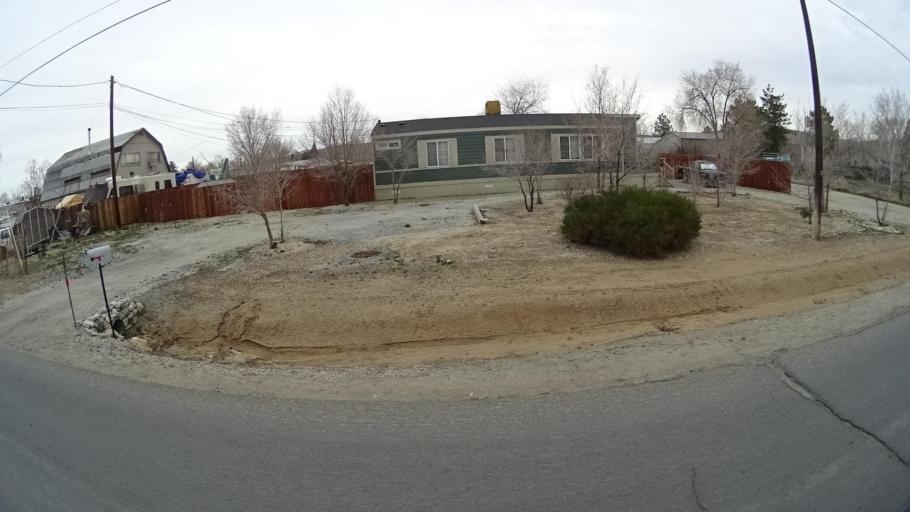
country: US
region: Nevada
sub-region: Washoe County
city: Sun Valley
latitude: 39.5974
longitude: -119.7711
